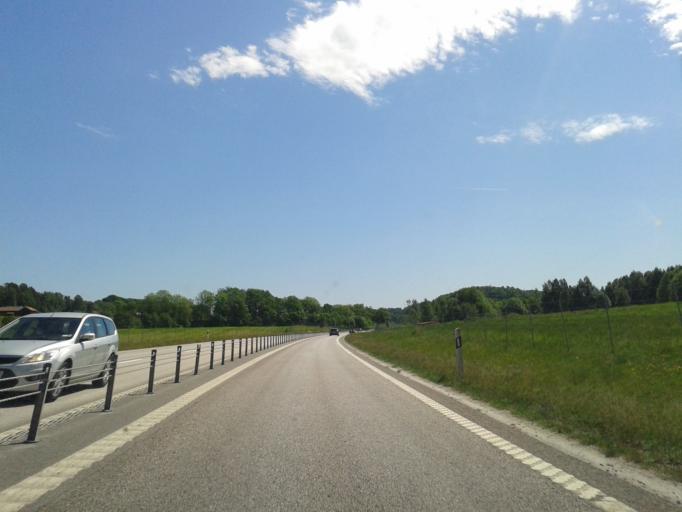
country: SE
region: Vaestra Goetaland
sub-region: Orust
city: Henan
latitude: 58.3508
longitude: 11.7407
